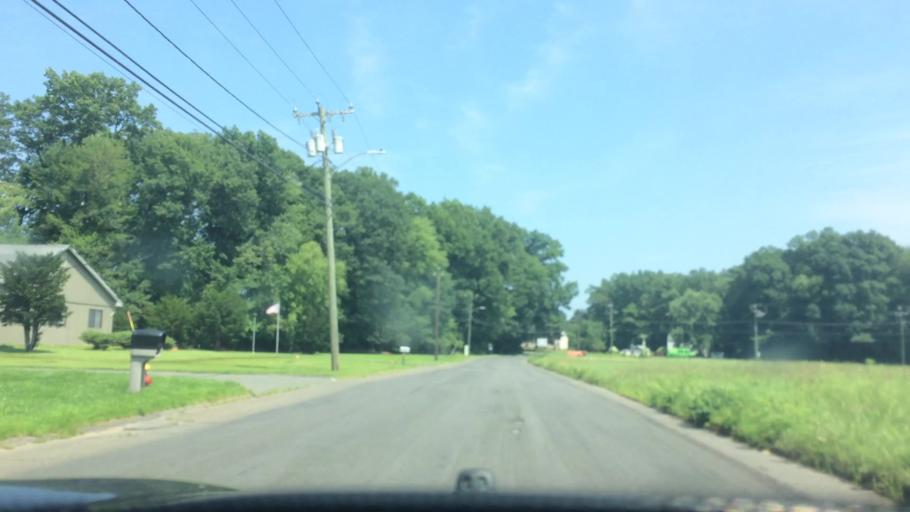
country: US
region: Connecticut
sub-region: Hartford County
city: Blue Hills
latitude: 41.8576
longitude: -72.7317
